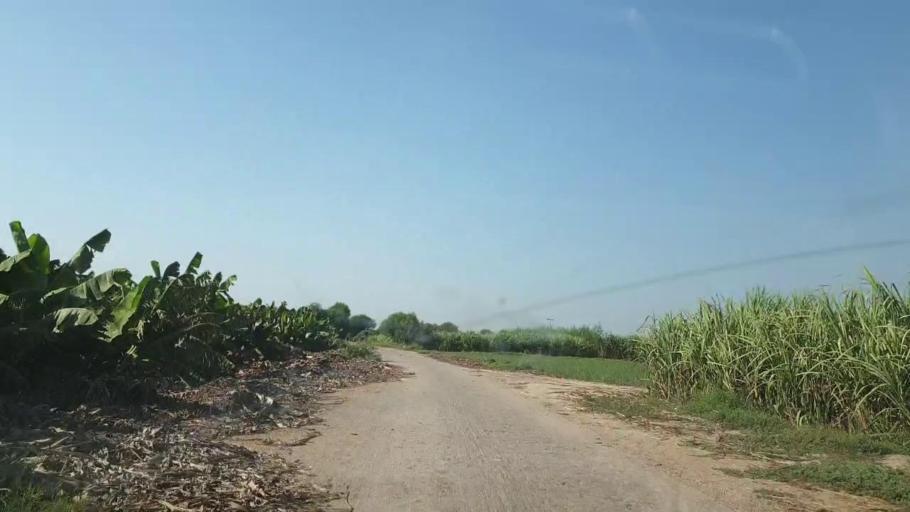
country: PK
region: Sindh
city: Tando Jam
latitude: 25.3413
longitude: 68.5862
